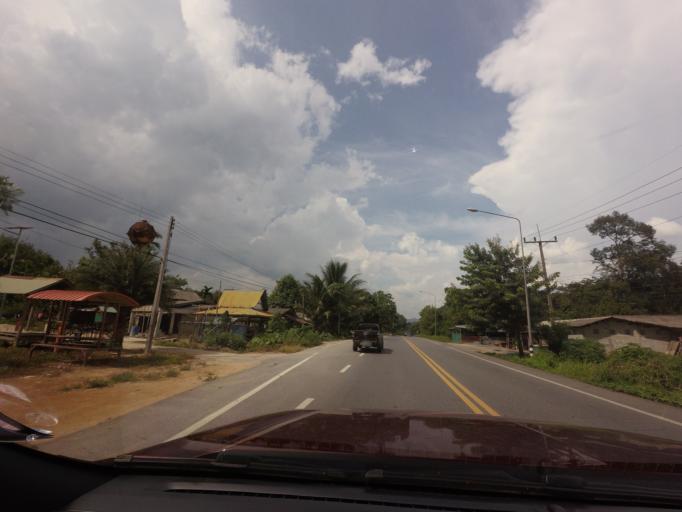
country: TH
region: Yala
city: Ban Nang Sata
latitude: 6.2520
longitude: 101.2236
